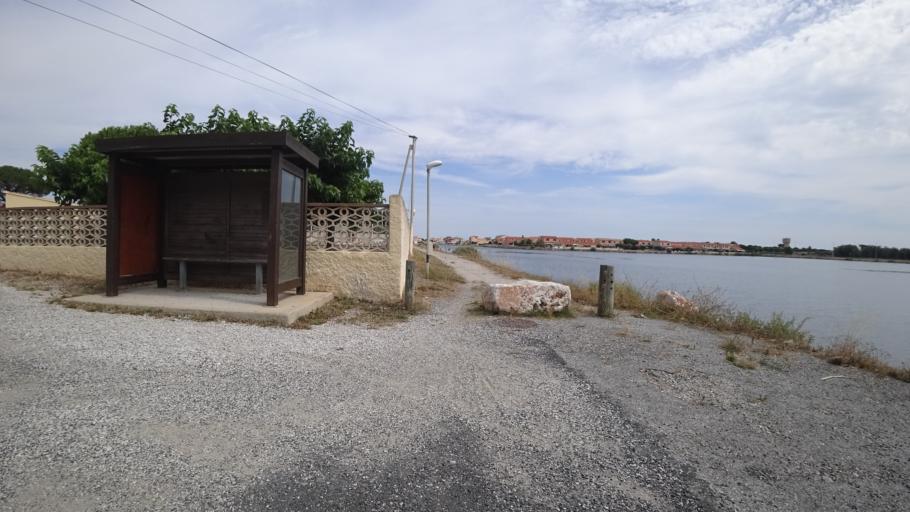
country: FR
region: Languedoc-Roussillon
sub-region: Departement des Pyrenees-Orientales
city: Le Barcares
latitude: 42.8060
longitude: 3.0269
